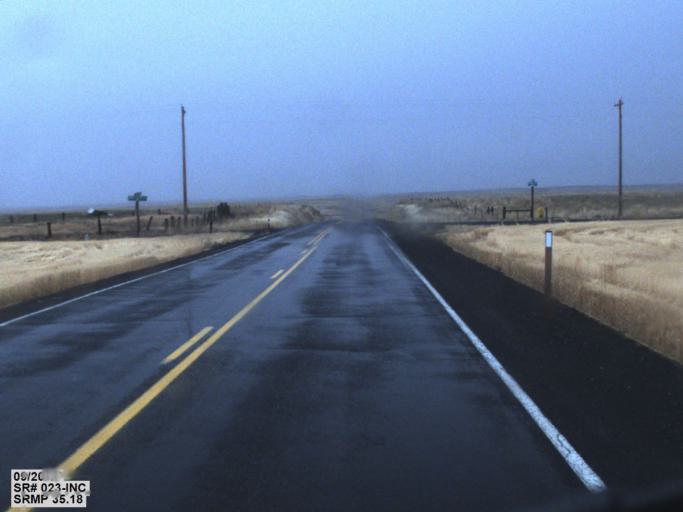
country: US
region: Washington
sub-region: Spokane County
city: Medical Lake
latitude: 47.2089
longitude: -117.8900
